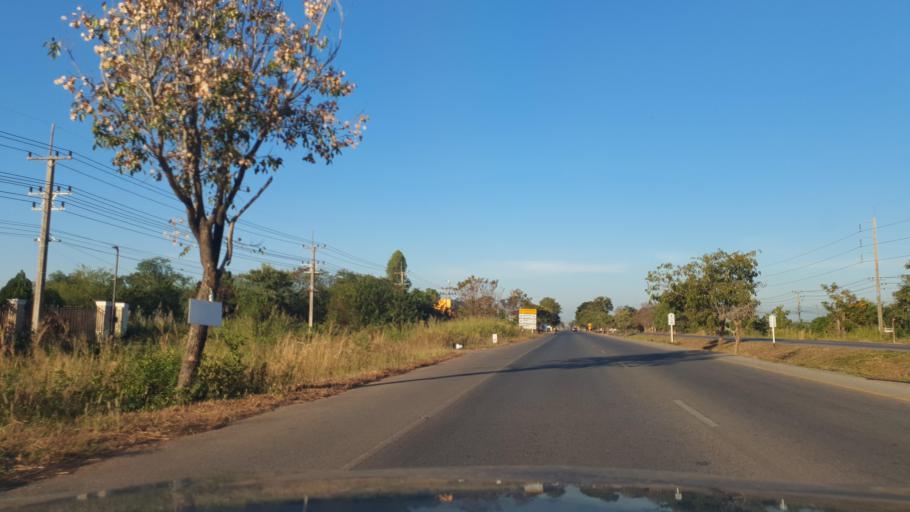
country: TH
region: Phitsanulok
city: Phitsanulok
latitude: 16.8641
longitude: 100.2858
